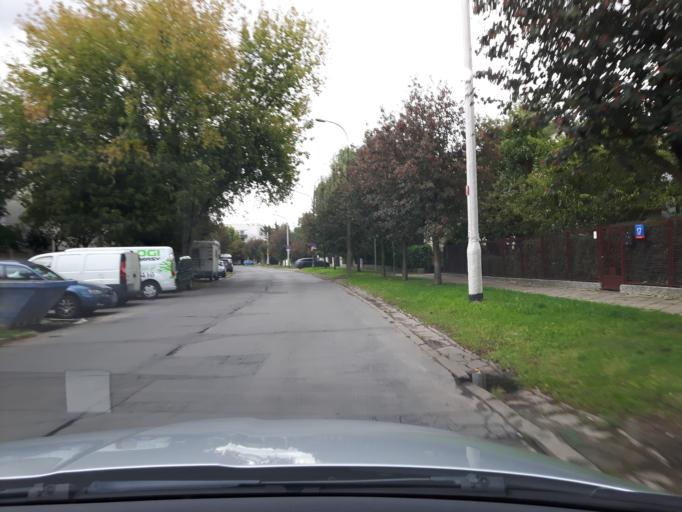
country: PL
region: Masovian Voivodeship
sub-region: Warszawa
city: Praga Poludnie
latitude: 52.2246
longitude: 21.0634
